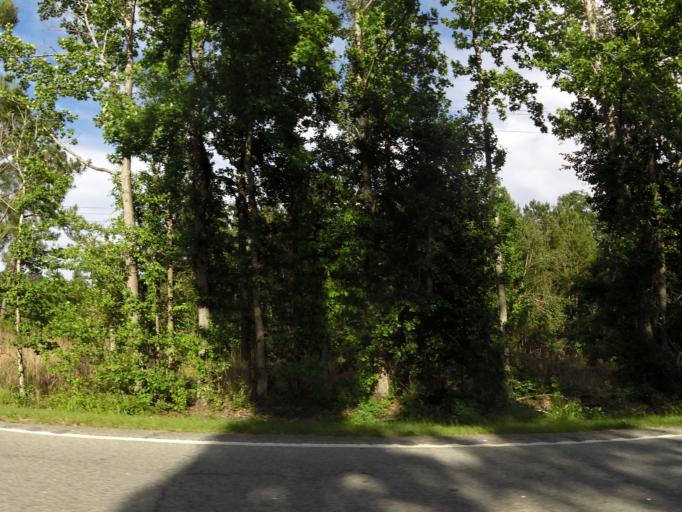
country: US
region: South Carolina
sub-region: Allendale County
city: Fairfax
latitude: 32.8754
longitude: -81.2384
